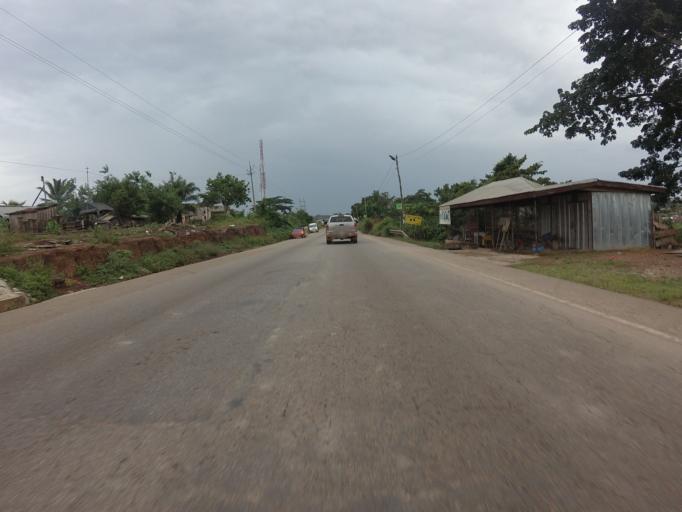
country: GH
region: Ashanti
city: Konongo
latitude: 6.6240
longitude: -1.2037
